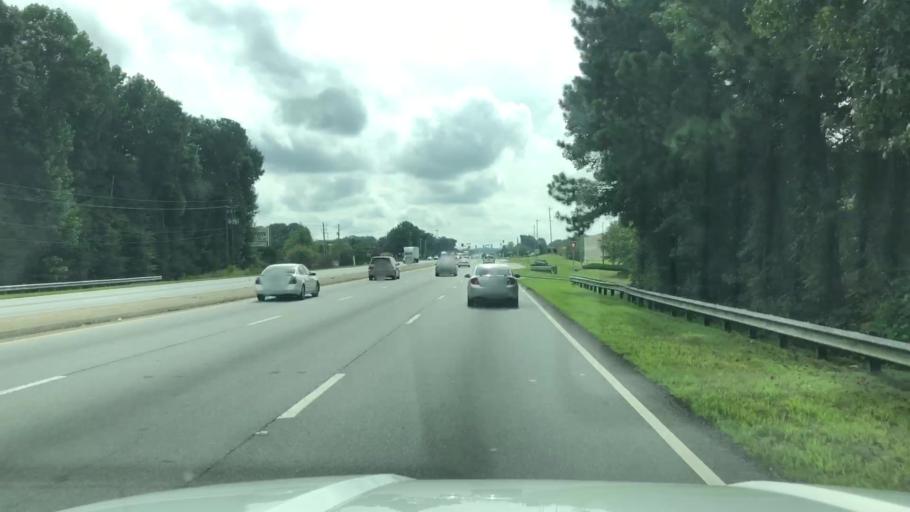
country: US
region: Georgia
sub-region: Cobb County
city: Austell
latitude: 33.7950
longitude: -84.6375
